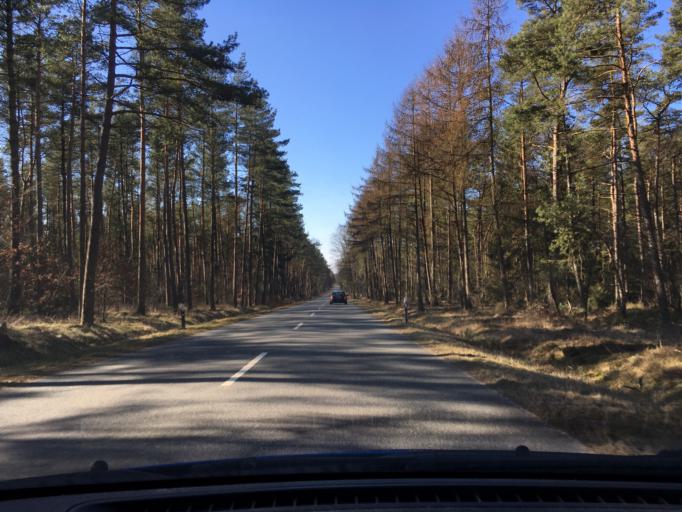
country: DE
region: Lower Saxony
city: Soderstorf
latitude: 53.1628
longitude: 10.1134
